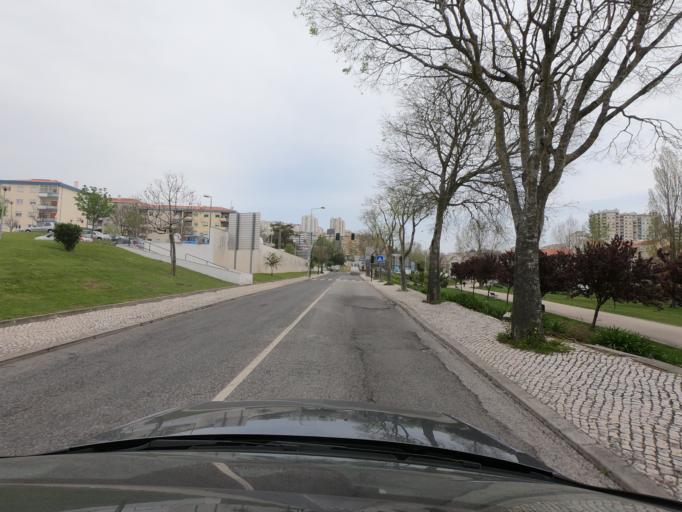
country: PT
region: Lisbon
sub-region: Sintra
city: Queluz
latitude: 38.7562
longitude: -9.2597
